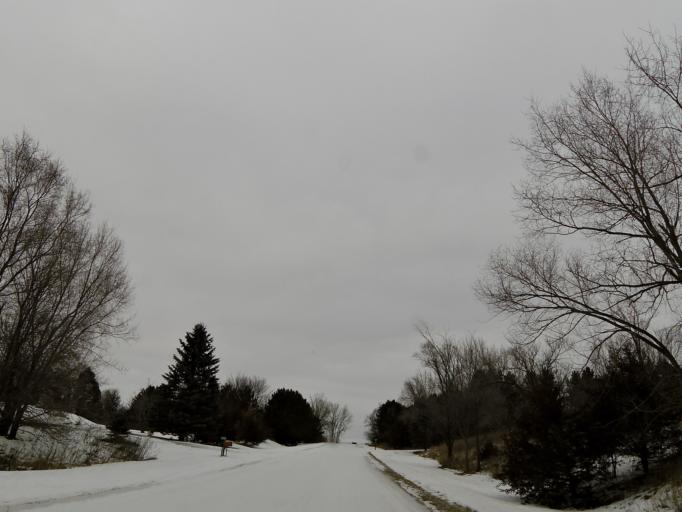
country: US
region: Wisconsin
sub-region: Pierce County
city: Prescott
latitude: 44.7953
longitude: -92.8244
